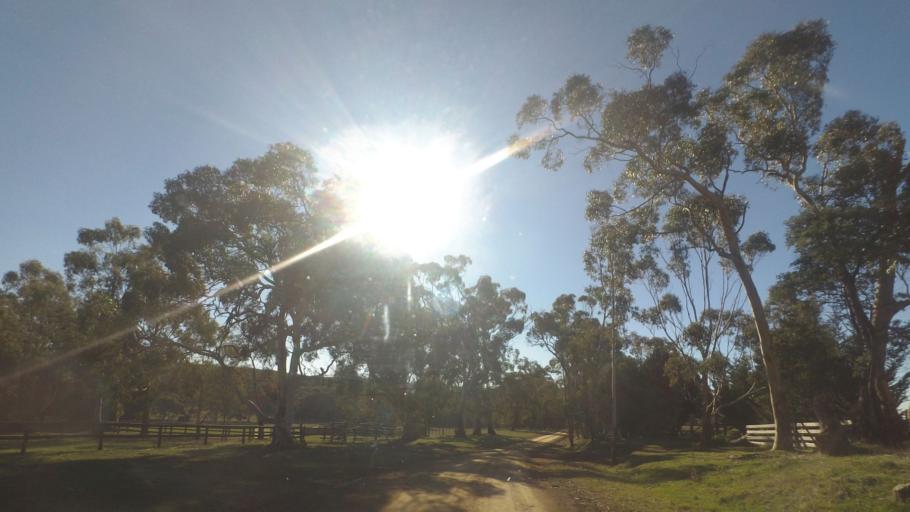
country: AU
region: Victoria
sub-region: Mount Alexander
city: Castlemaine
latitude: -37.2936
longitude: 144.3307
